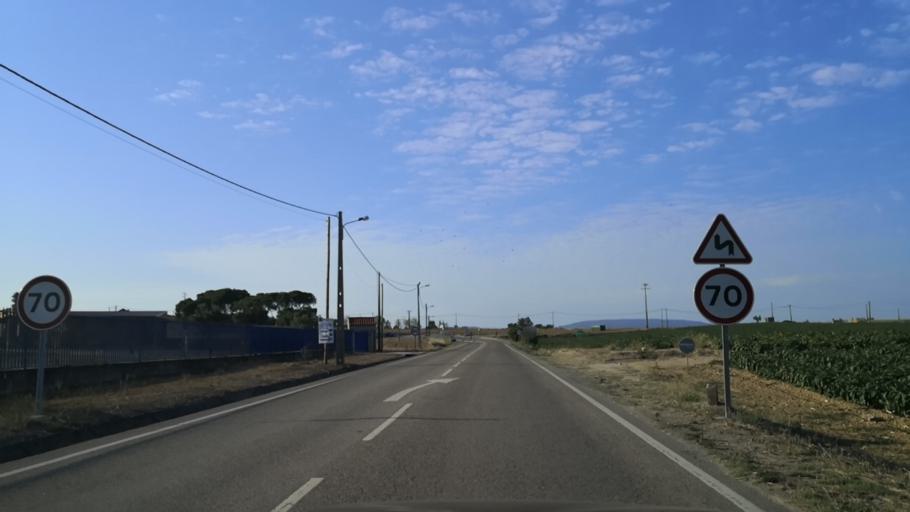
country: PT
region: Santarem
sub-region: Santarem
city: Santarem
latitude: 39.3442
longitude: -8.6610
